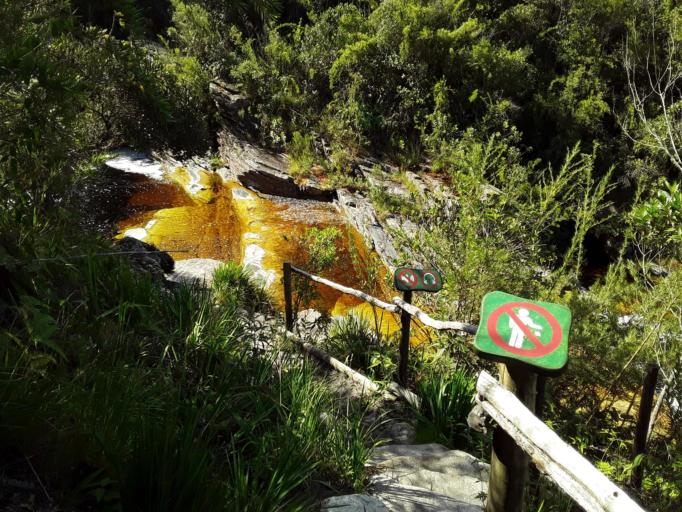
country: BR
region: Minas Gerais
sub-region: Lima Duarte
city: Lima Duarte
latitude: -21.7140
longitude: -43.8943
